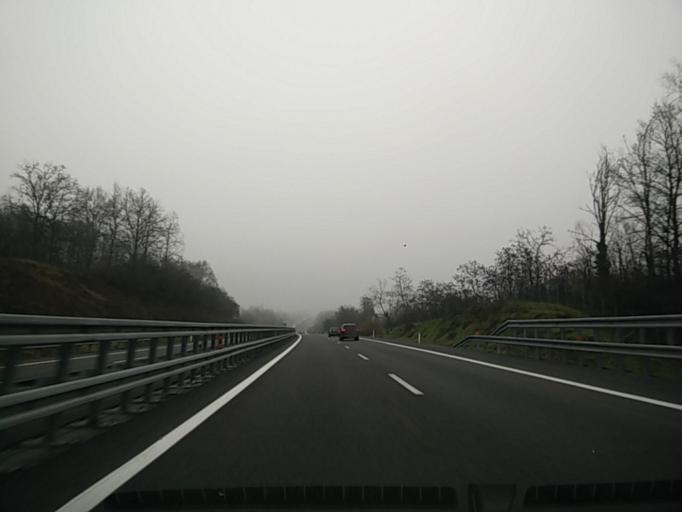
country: IT
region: Piedmont
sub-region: Provincia di Asti
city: Baldichieri d'Asti
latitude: 44.9017
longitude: 8.1359
